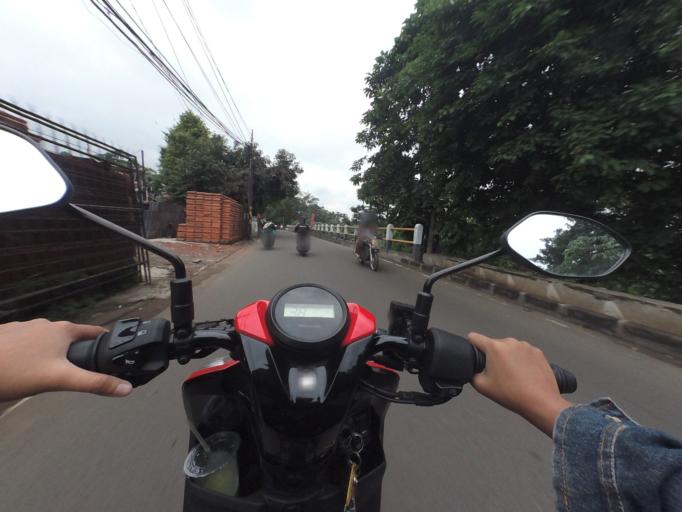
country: ID
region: West Java
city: Bogor
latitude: -6.5629
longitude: 106.8021
